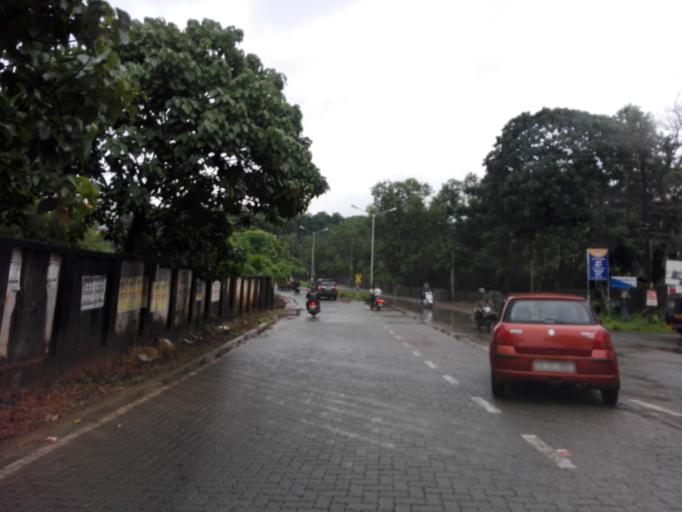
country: IN
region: Kerala
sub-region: Ernakulam
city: Aluva
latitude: 10.0532
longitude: 76.3526
